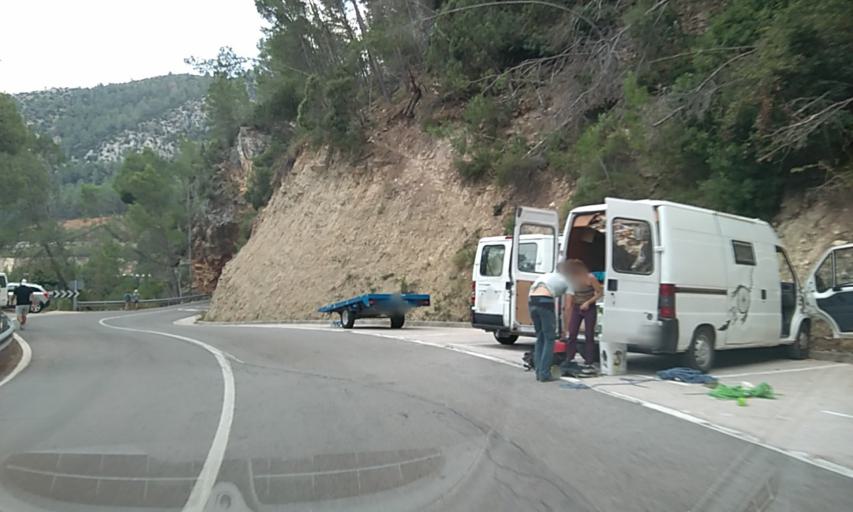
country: ES
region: Valencia
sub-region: Provincia de Castello
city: Montanejos
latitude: 40.0770
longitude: -0.5395
